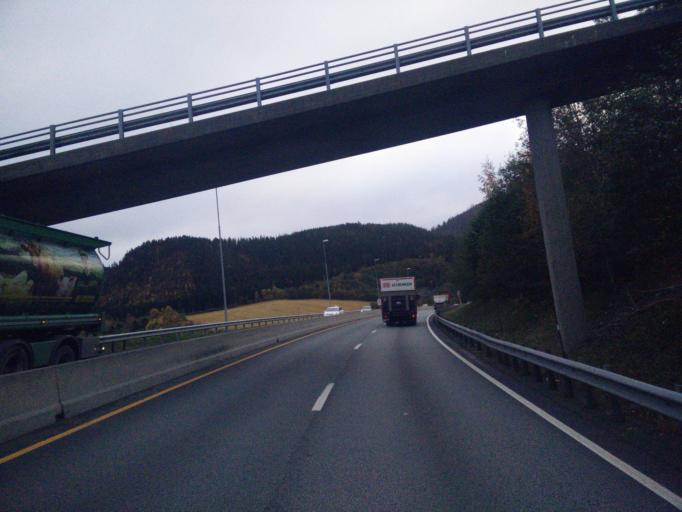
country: NO
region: Sor-Trondelag
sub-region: Malvik
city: Malvik
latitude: 63.4255
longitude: 10.5717
